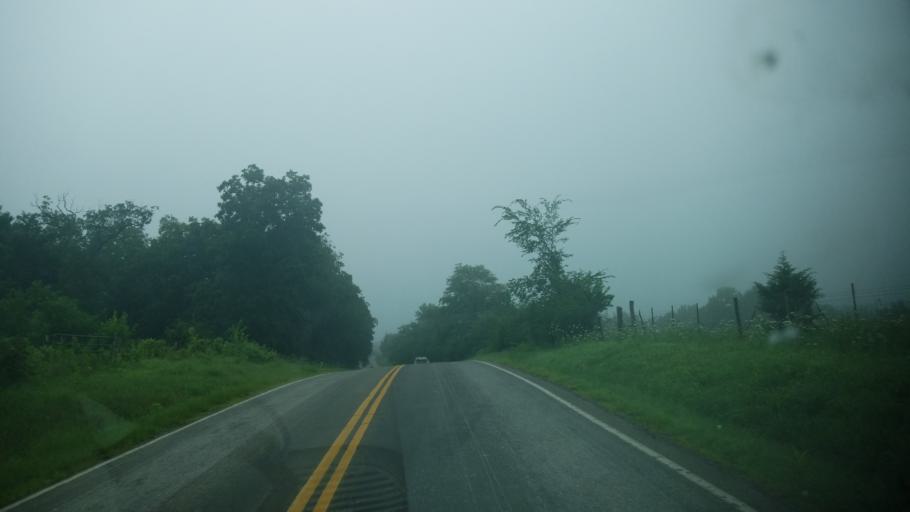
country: US
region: Missouri
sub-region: Audrain County
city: Vandalia
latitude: 39.3184
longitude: -91.3451
